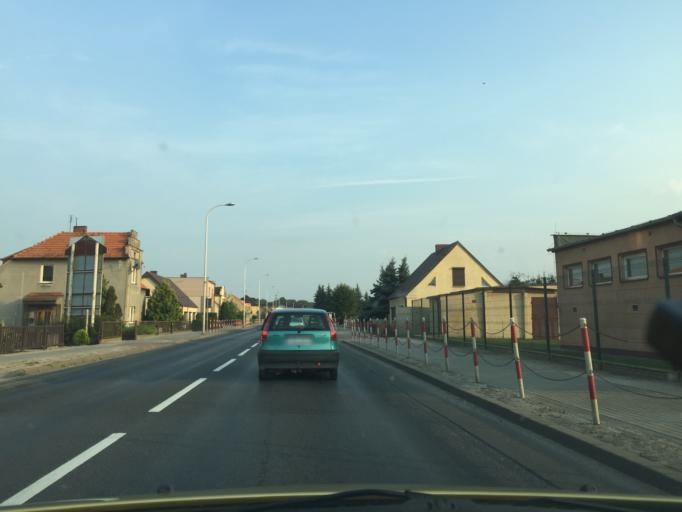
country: PL
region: Greater Poland Voivodeship
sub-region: Powiat jarocinski
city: Jarocin
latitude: 51.9612
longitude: 17.5133
